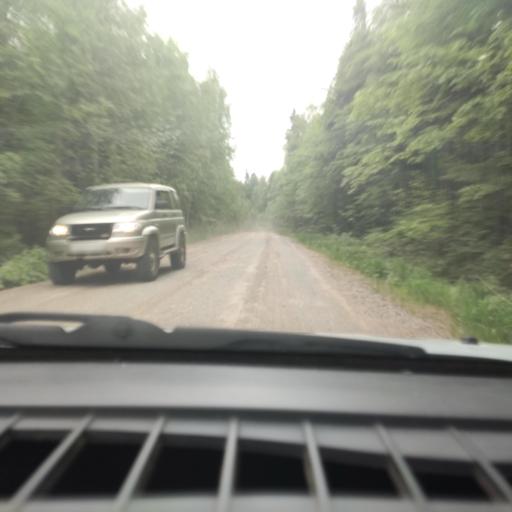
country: RU
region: Perm
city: Novyye Lyady
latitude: 57.9005
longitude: 56.6521
